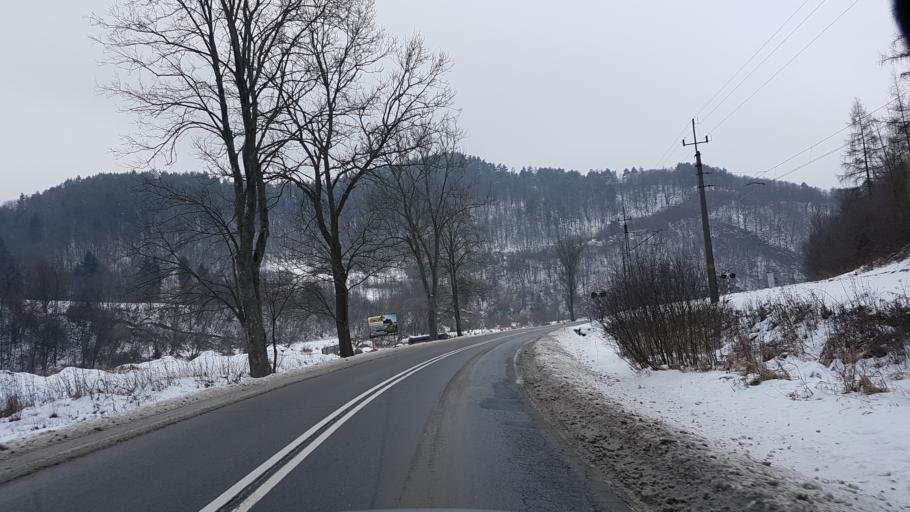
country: PL
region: Lesser Poland Voivodeship
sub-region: Powiat nowosadecki
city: Piwniczna-Zdroj
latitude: 49.3903
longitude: 20.7494
